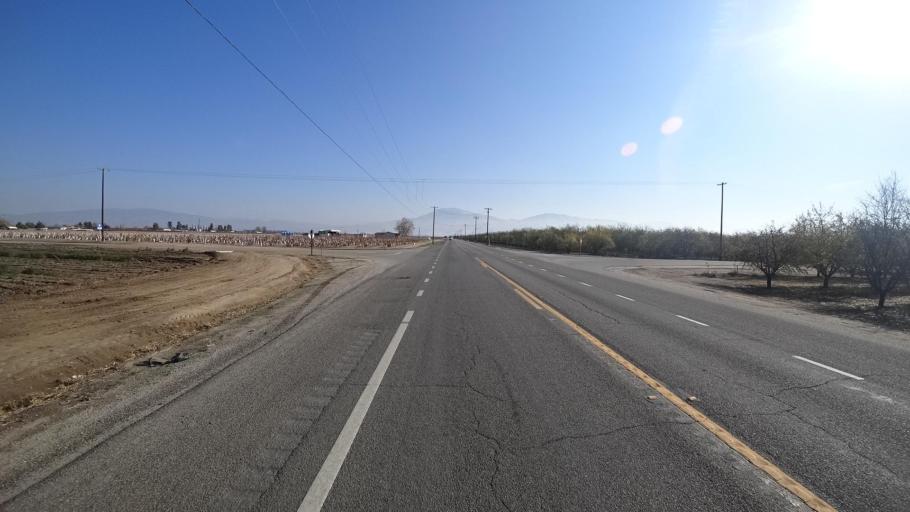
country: US
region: California
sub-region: Kern County
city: Weedpatch
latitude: 35.2094
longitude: -118.8959
